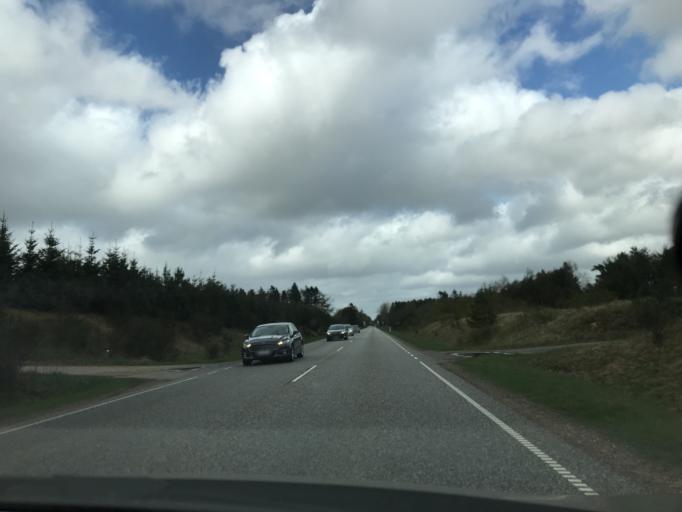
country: DK
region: Central Jutland
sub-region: Herning Kommune
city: Sunds
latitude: 56.3789
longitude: 8.9874
